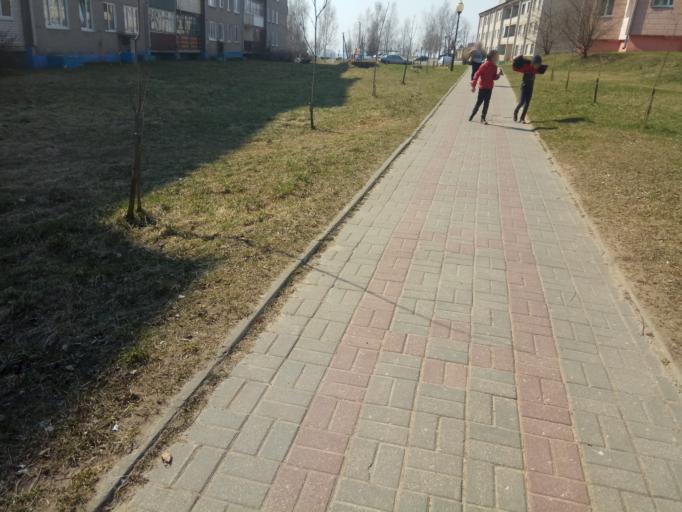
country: BY
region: Minsk
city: Valozhyn
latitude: 54.0871
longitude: 26.5204
